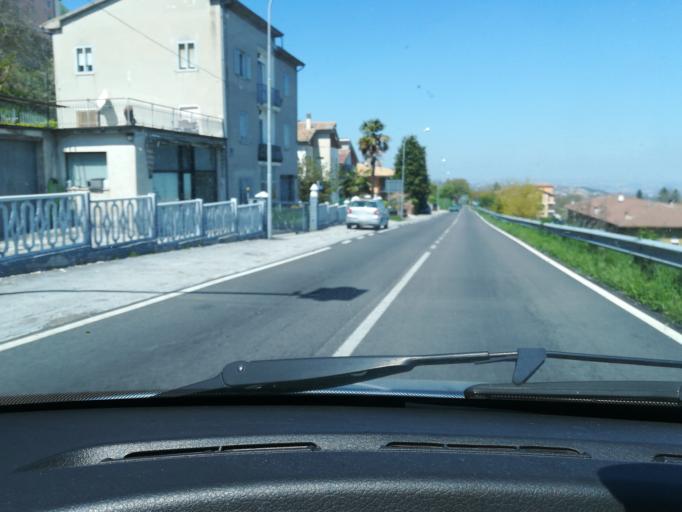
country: IT
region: The Marches
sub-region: Provincia di Macerata
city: Cingoli
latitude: 43.3758
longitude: 13.2181
